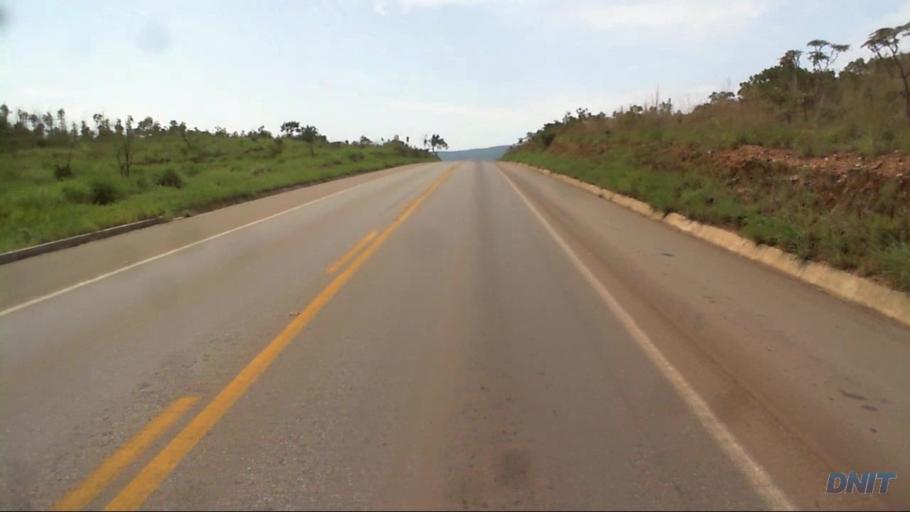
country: BR
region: Goias
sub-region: Barro Alto
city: Barro Alto
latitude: -15.1703
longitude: -48.7965
